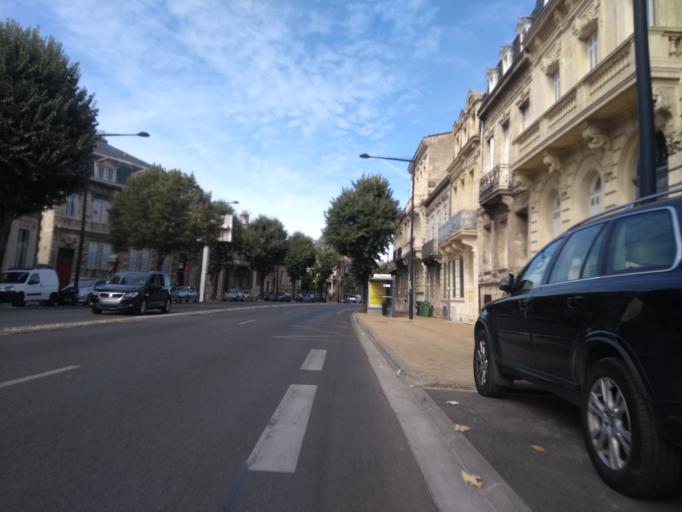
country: FR
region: Aquitaine
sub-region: Departement de la Gironde
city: Bordeaux
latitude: 44.8426
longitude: -0.5994
